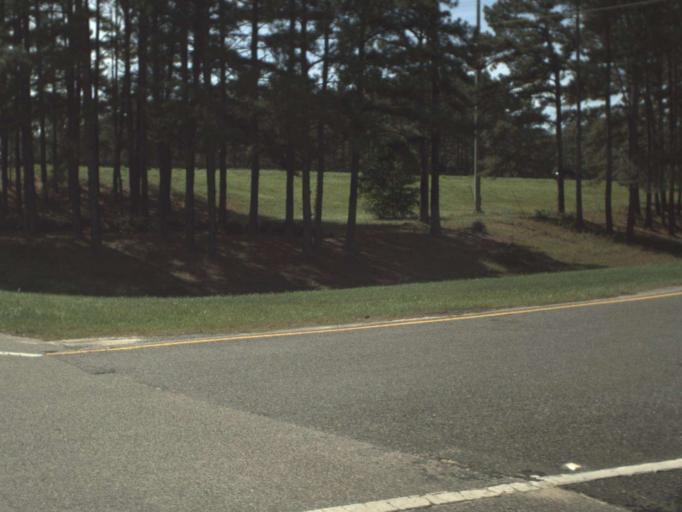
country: US
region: Florida
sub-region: Washington County
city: Chipley
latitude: 30.7489
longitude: -85.5516
